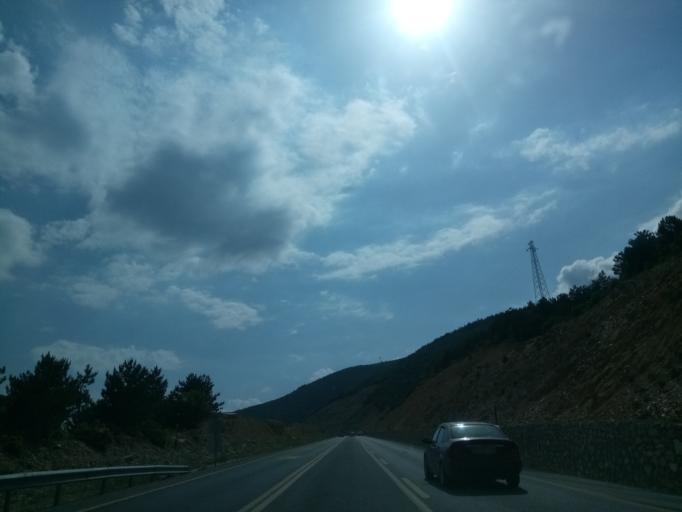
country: TR
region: Konya
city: Aksehir
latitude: 38.3023
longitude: 31.4590
